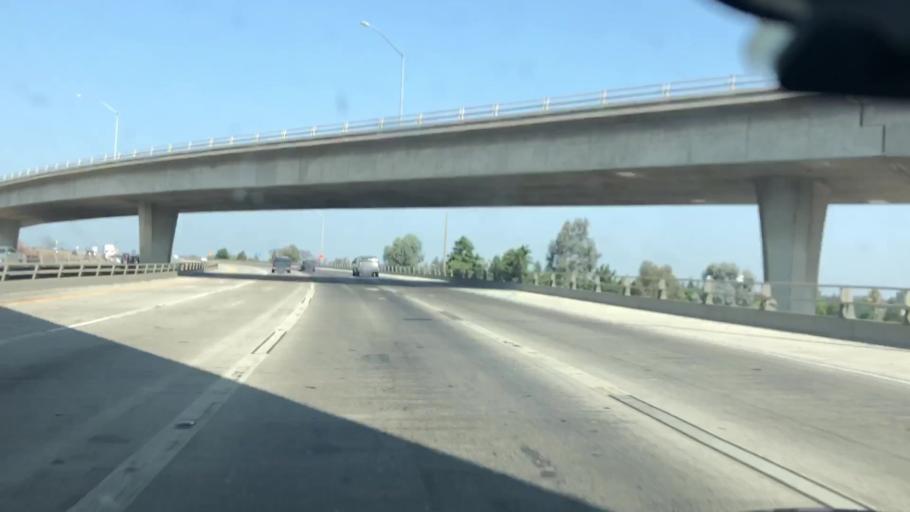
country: US
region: California
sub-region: San Joaquin County
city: Stockton
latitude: 37.9479
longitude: -121.3001
